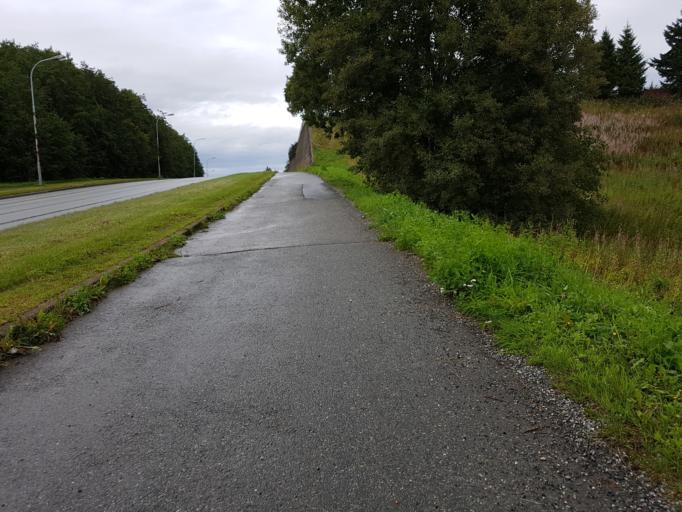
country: NO
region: Sor-Trondelag
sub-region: Trondheim
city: Trondheim
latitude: 63.3941
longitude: 10.4024
